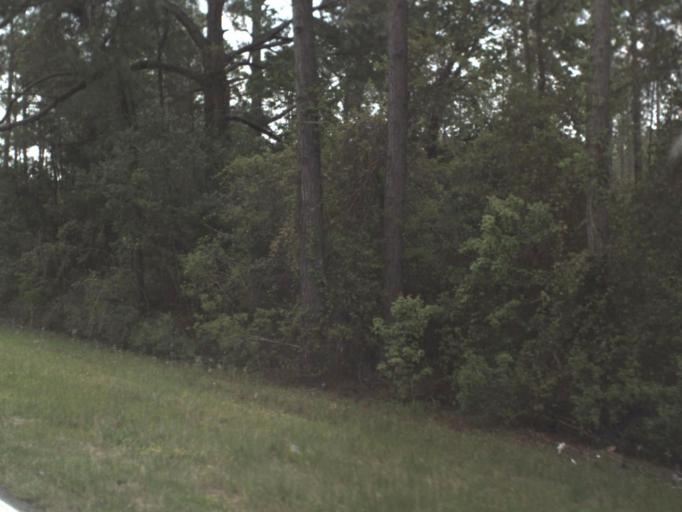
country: US
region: Florida
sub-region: Escambia County
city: Myrtle Grove
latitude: 30.3532
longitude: -87.3786
